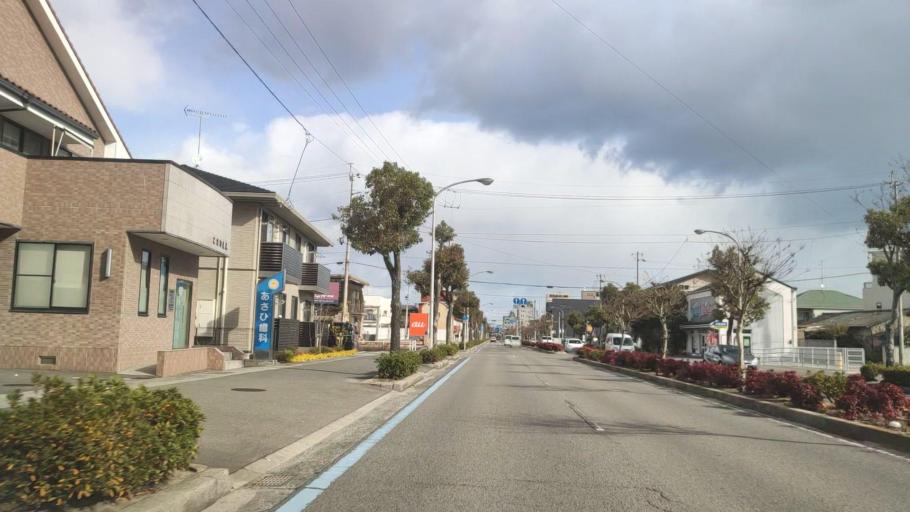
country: JP
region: Ehime
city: Hojo
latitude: 34.0616
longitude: 132.9854
